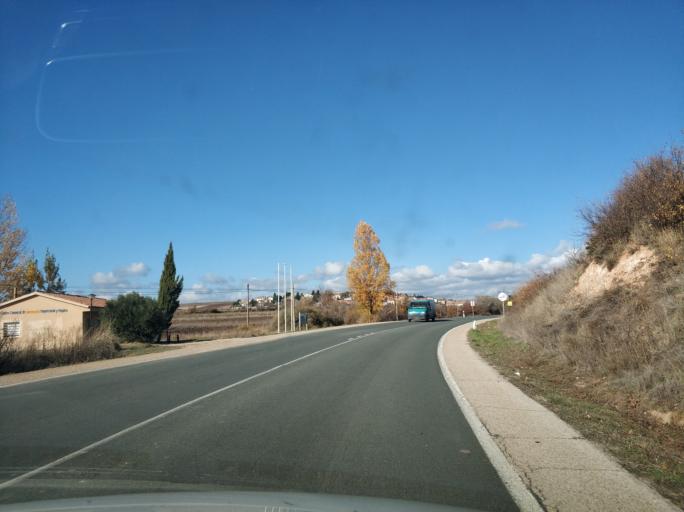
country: ES
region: Castille and Leon
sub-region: Provincia de Soria
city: Almazan
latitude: 41.4751
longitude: -2.5300
